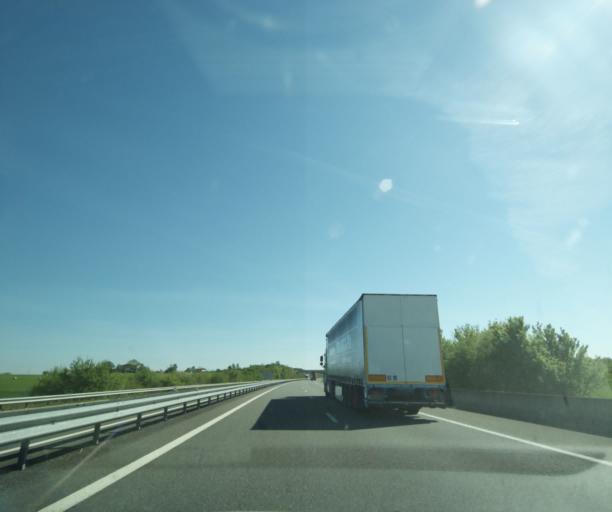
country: FR
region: Midi-Pyrenees
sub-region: Departement du Tarn-et-Garonne
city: Caussade
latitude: 44.2108
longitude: 1.5416
